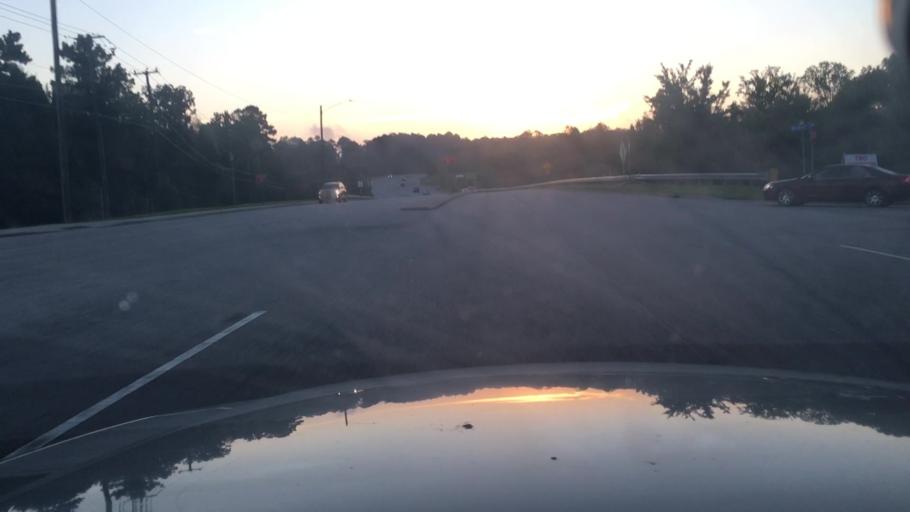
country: US
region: North Carolina
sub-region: Hoke County
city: Rockfish
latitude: 35.0626
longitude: -79.0404
